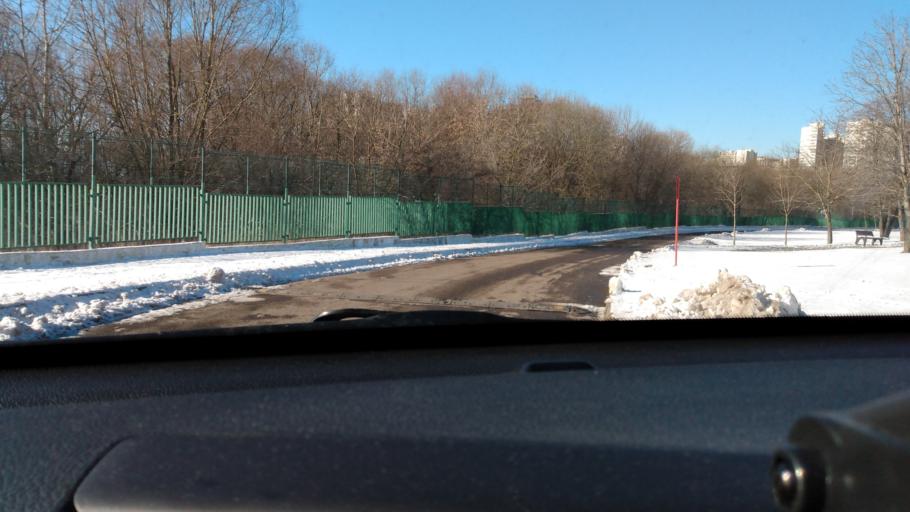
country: RU
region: Moscow
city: Nikol'skoye
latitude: 55.6702
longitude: 37.4888
